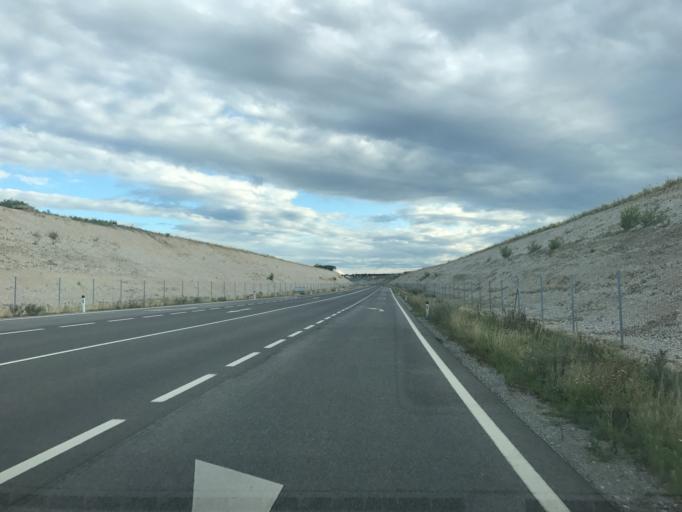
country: AT
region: Lower Austria
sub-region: Politischer Bezirk Wiener Neustadt
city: Sollenau
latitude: 47.8901
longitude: 16.2685
